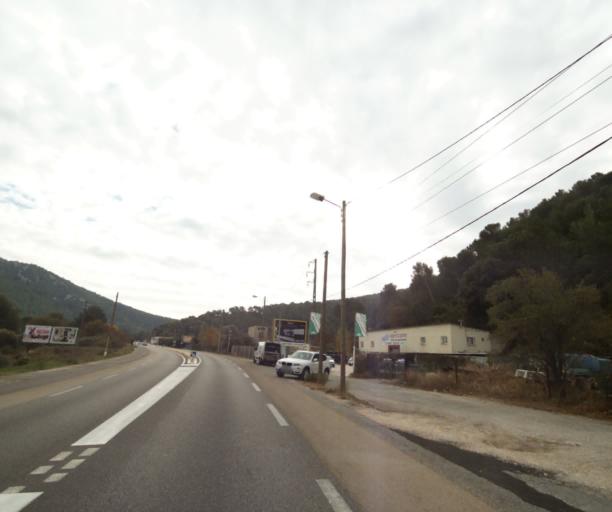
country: FR
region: Provence-Alpes-Cote d'Azur
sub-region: Departement des Bouches-du-Rhone
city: Gemenos
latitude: 43.2750
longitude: 5.6333
